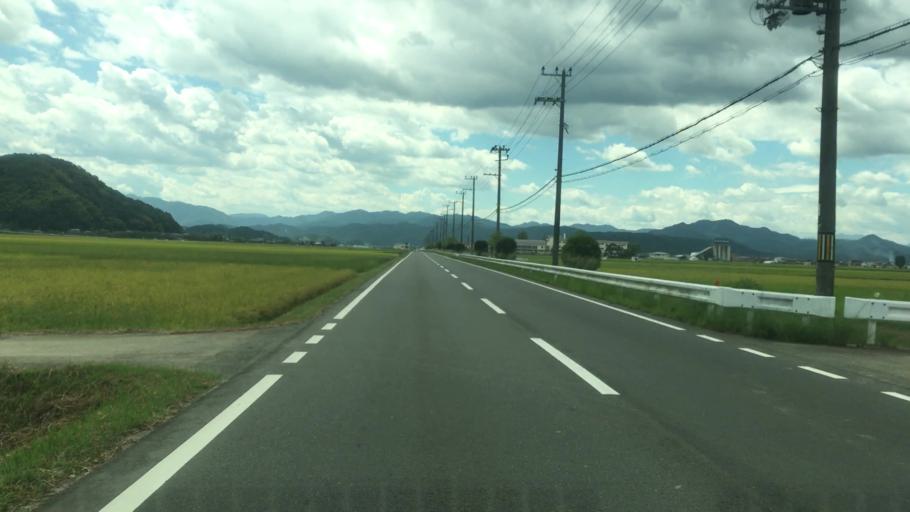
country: JP
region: Hyogo
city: Toyooka
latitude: 35.5372
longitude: 134.8397
